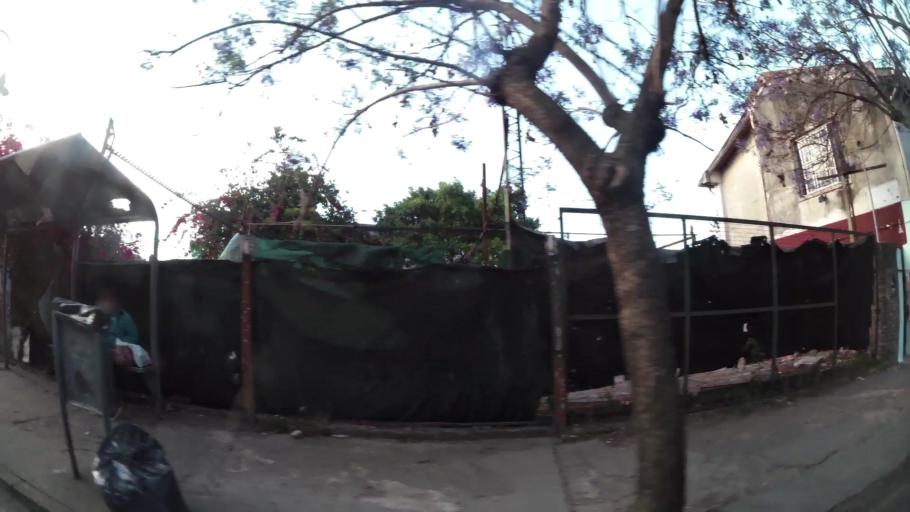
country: AR
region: Buenos Aires
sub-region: Partido de Tigre
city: Tigre
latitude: -34.4515
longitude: -58.5723
